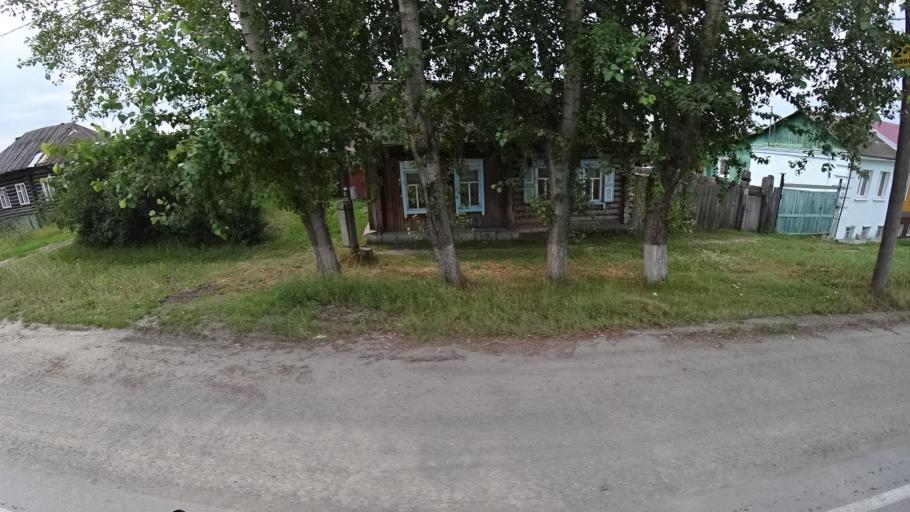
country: RU
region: Sverdlovsk
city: Kamyshlov
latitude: 56.8471
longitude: 62.6745
